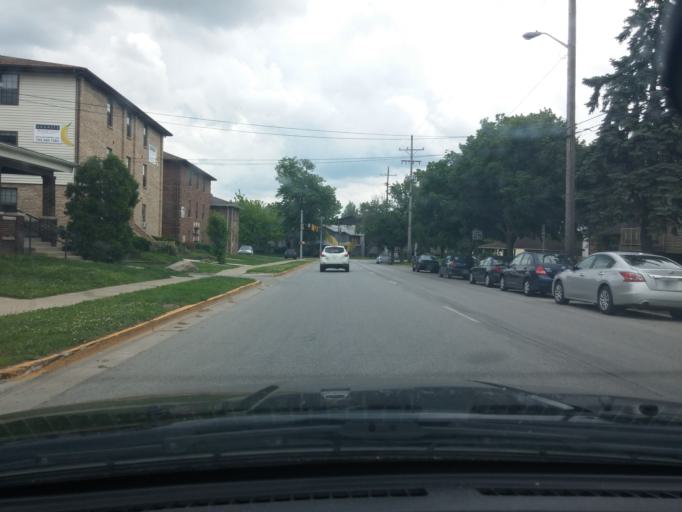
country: US
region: Indiana
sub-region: Tippecanoe County
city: West Lafayette
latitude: 40.4221
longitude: -86.9089
